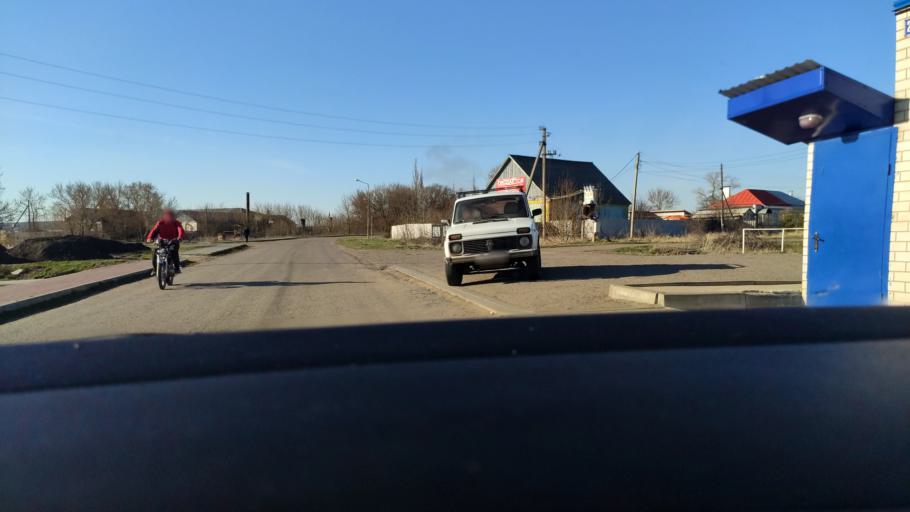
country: RU
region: Voronezj
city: Maslovka
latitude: 51.5024
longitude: 39.2941
